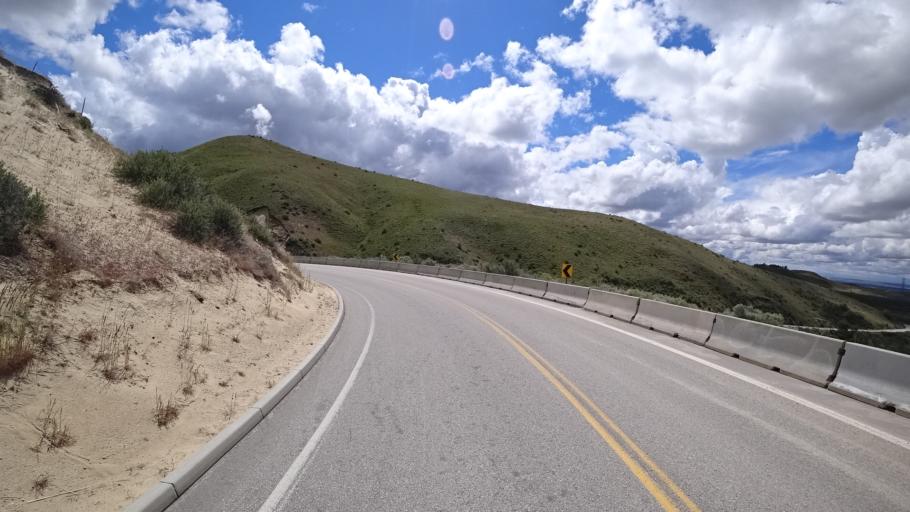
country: US
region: Idaho
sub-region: Ada County
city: Boise
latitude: 43.6825
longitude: -116.1822
